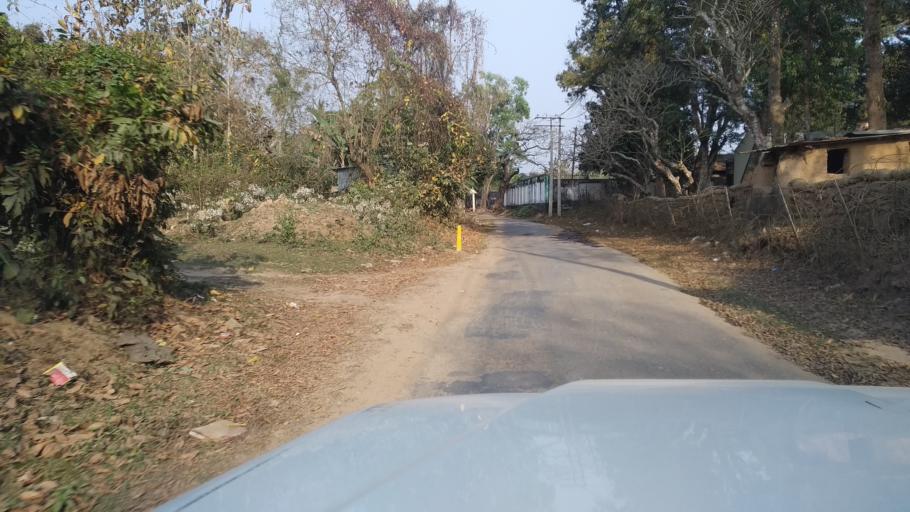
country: IN
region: Tripura
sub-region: West Tripura
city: Sonamura
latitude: 23.4189
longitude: 91.2849
